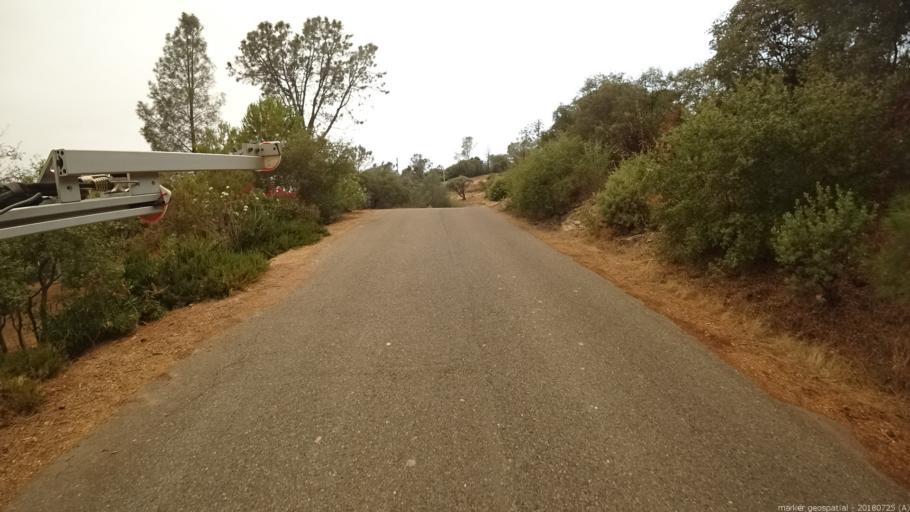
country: US
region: California
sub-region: Madera County
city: Coarsegold
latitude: 37.1888
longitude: -119.6757
